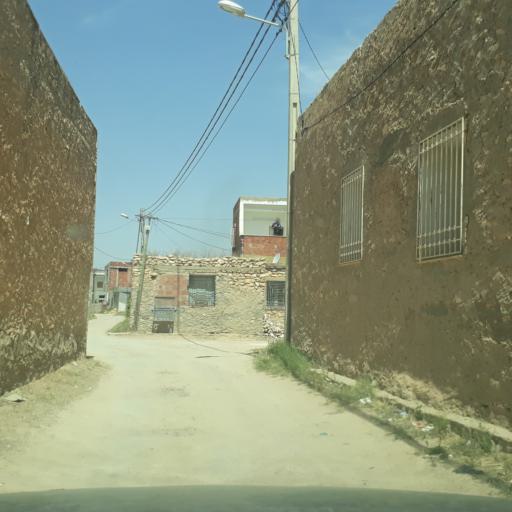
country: TN
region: Safaqis
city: Al Qarmadah
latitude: 34.8228
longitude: 10.7796
